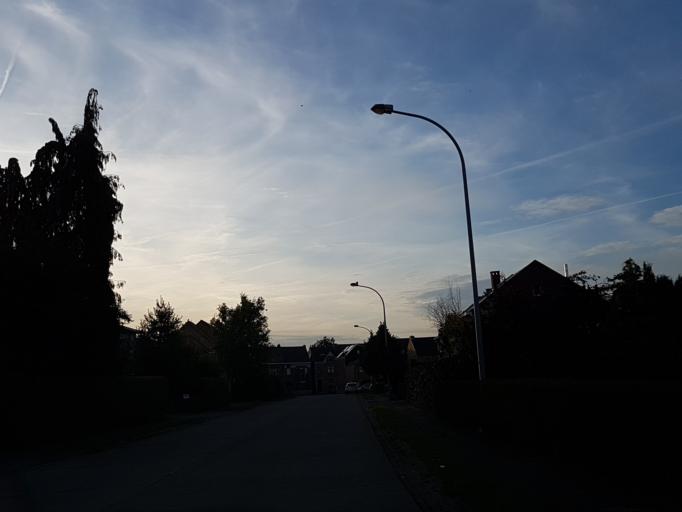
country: BE
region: Flanders
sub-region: Provincie Vlaams-Brabant
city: Londerzeel
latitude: 51.0043
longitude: 4.3105
